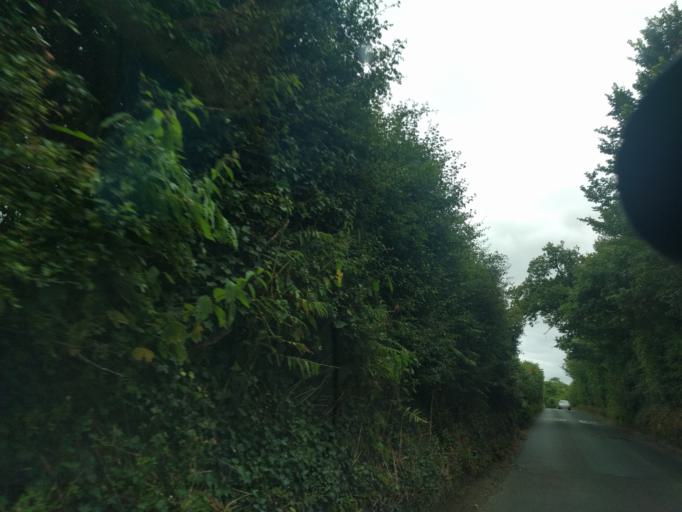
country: GB
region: England
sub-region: Wiltshire
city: Market Lavington
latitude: 51.2817
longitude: -2.0095
